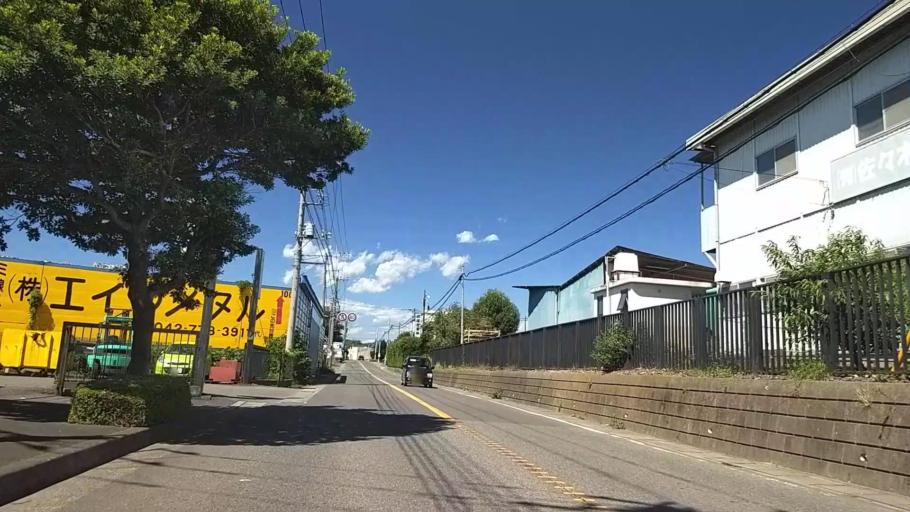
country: JP
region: Kanagawa
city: Zama
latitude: 35.5348
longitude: 139.3499
